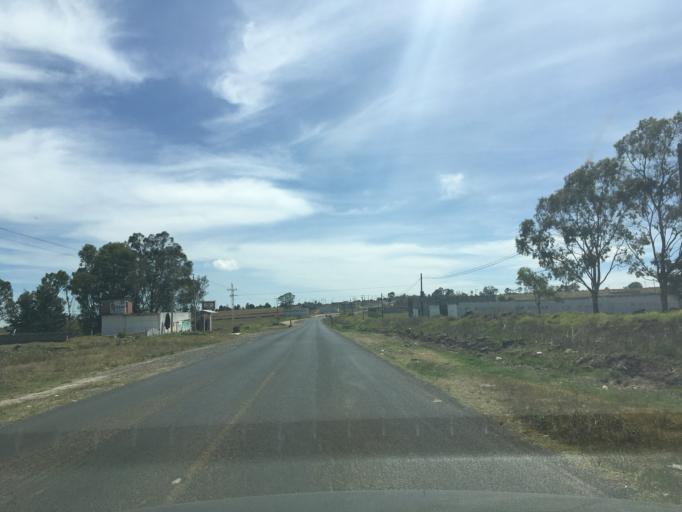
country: MX
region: Queretaro
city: Amealco
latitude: 20.2045
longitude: -100.1301
